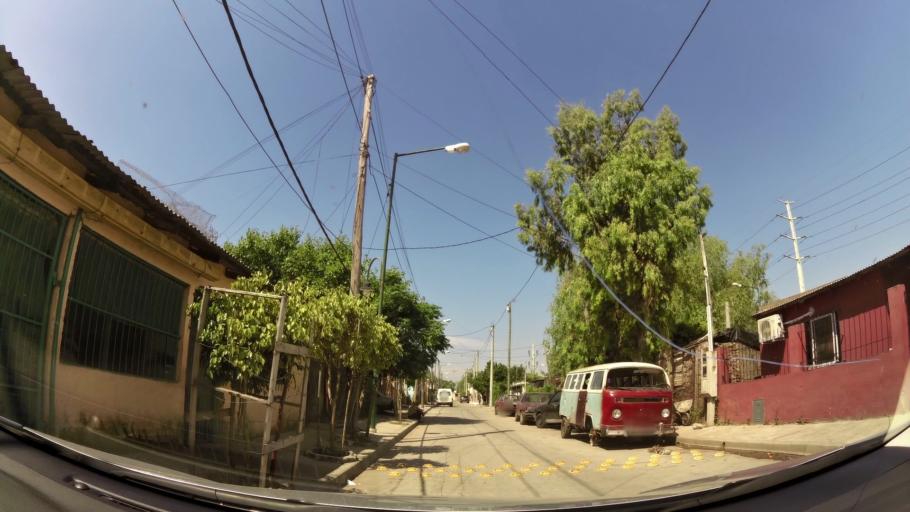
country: AR
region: Buenos Aires
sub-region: Partido de Tigre
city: Tigre
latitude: -34.4675
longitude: -58.5983
